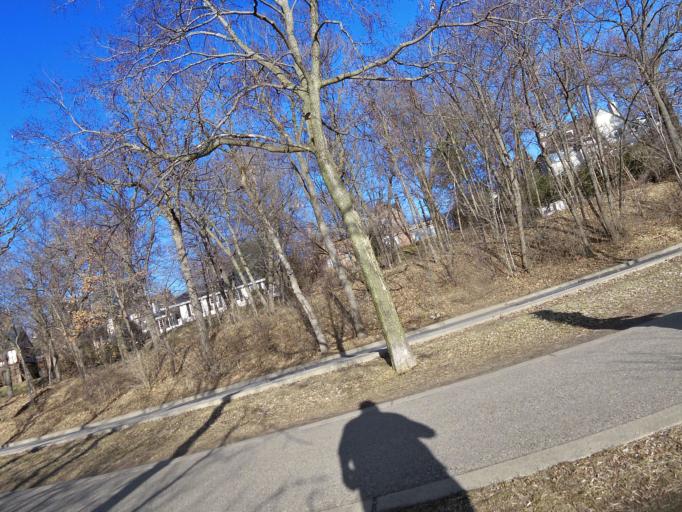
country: US
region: Minnesota
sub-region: Hennepin County
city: Richfield
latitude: 44.9238
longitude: -93.2968
